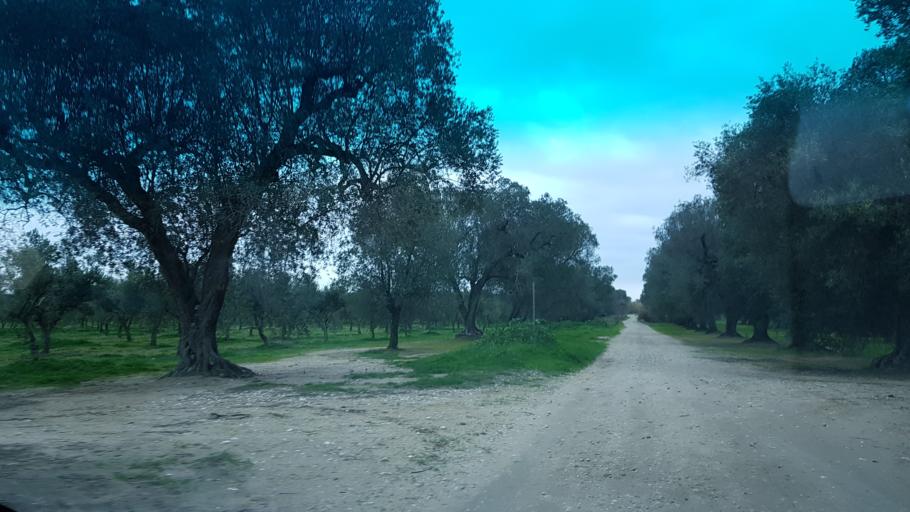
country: IT
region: Apulia
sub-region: Provincia di Brindisi
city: La Rosa
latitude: 40.5849
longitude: 17.9879
